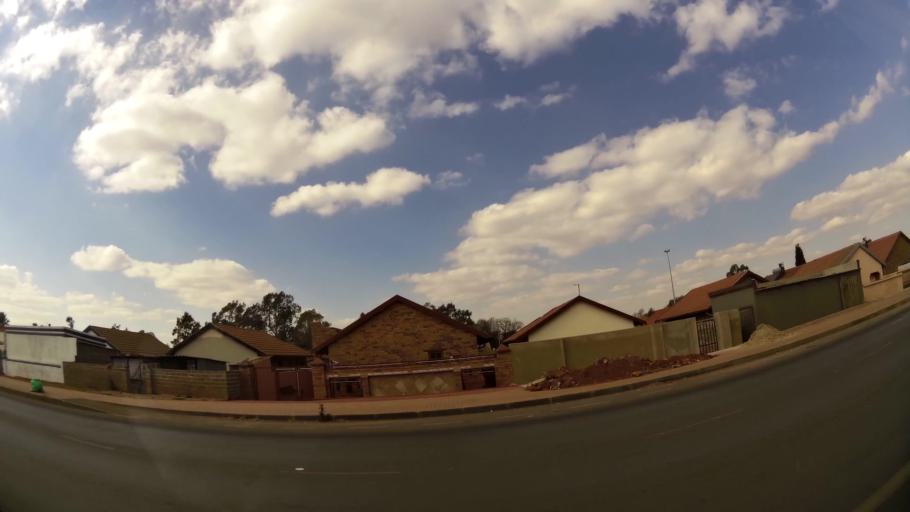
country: ZA
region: Gauteng
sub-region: Ekurhuleni Metropolitan Municipality
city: Tembisa
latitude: -25.9865
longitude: 28.2438
